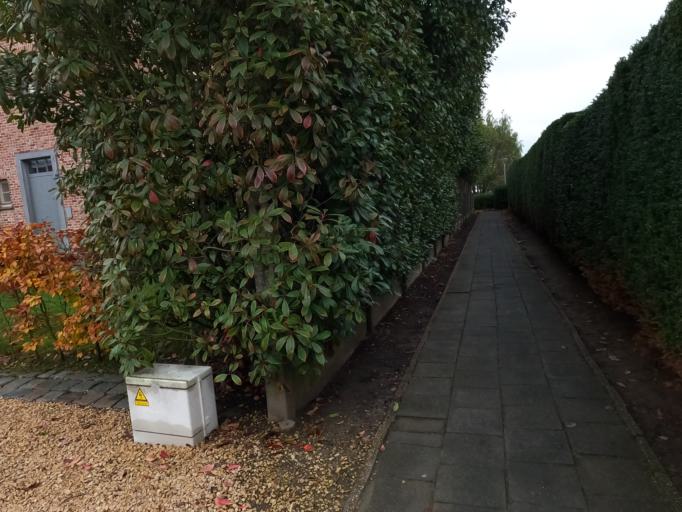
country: BE
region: Flanders
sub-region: Provincie Antwerpen
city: Nijlen
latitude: 51.1409
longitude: 4.6799
